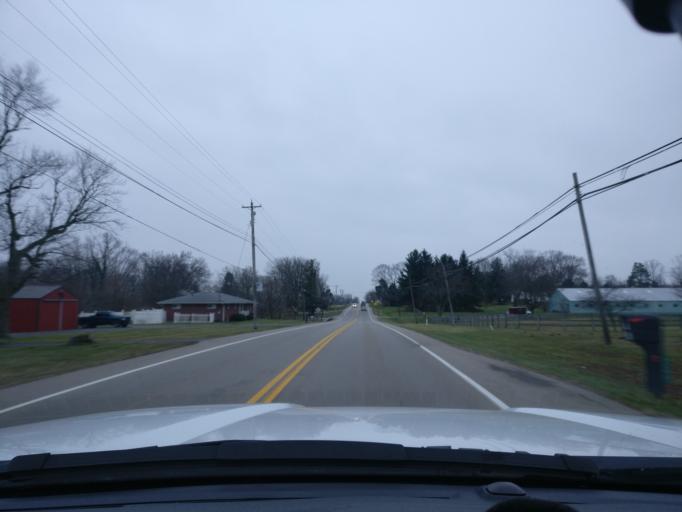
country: US
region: Ohio
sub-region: Warren County
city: Lebanon
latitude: 39.4762
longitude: -84.2021
